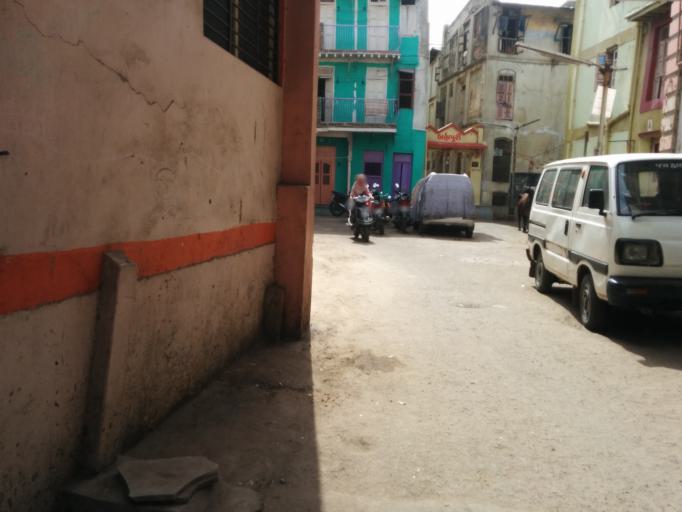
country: IN
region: Gujarat
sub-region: Ahmadabad
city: Ahmedabad
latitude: 23.0186
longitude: 72.5953
